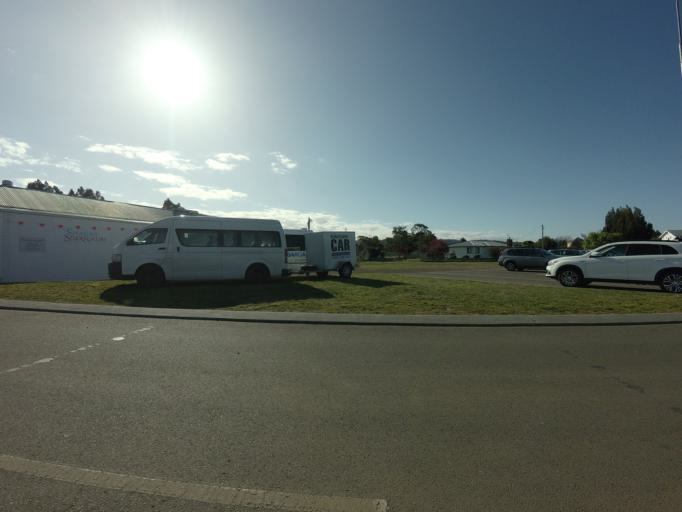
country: AU
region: Tasmania
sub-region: Sorell
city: Sorell
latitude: -42.5105
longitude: 147.9140
